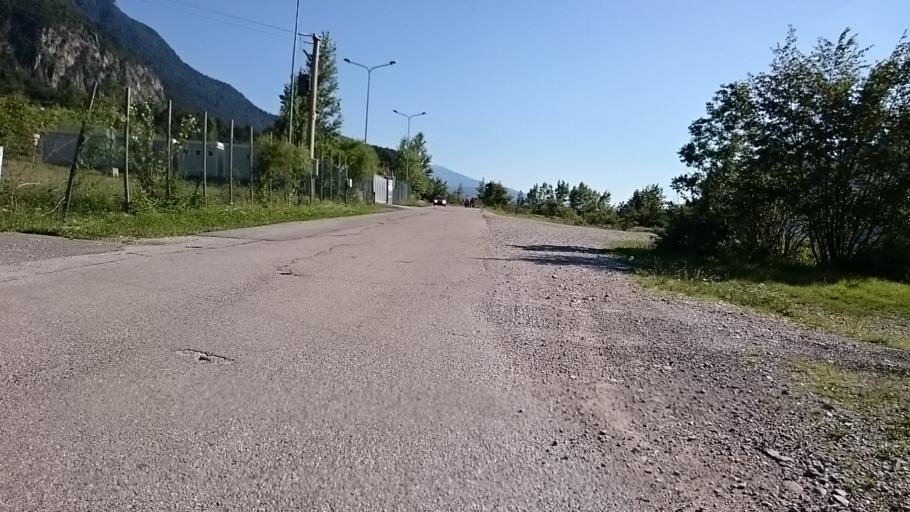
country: IT
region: Veneto
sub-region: Provincia di Belluno
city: Soverzene
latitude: 46.2227
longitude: 12.3011
